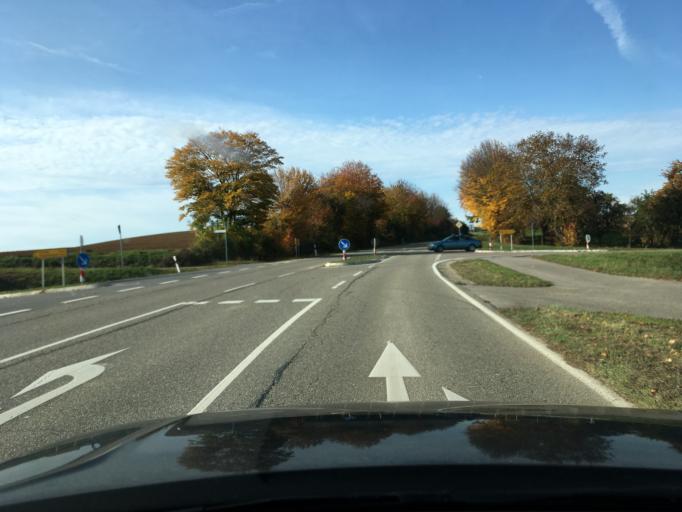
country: DE
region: Baden-Wuerttemberg
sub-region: Regierungsbezirk Stuttgart
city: Bad Rappenau
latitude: 49.2315
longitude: 9.0600
